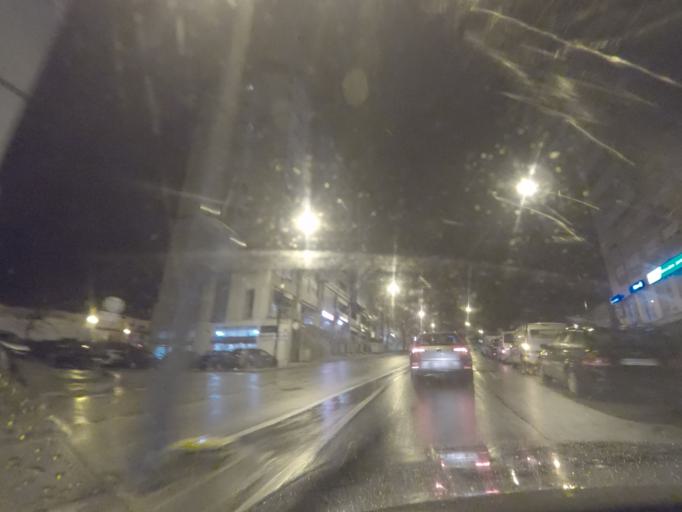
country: PT
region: Vila Real
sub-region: Vila Real
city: Vila Real
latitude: 41.2993
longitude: -7.7510
